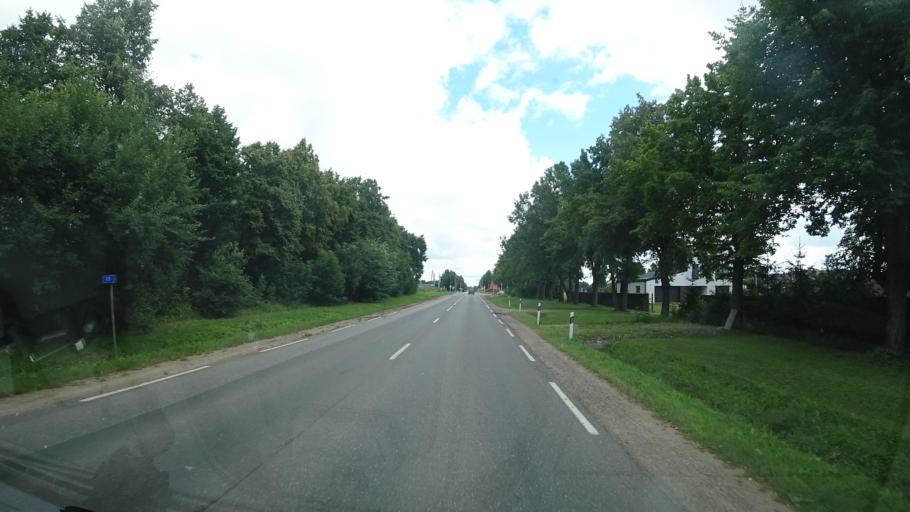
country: LT
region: Marijampoles apskritis
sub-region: Marijampole Municipality
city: Marijampole
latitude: 54.5253
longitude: 23.3244
